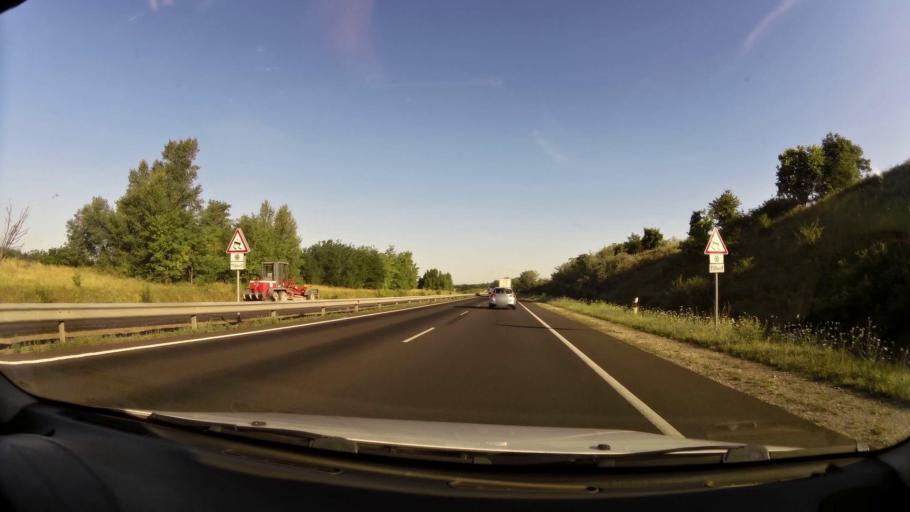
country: HU
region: Pest
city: Cegledbercel
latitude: 47.2383
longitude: 19.6623
